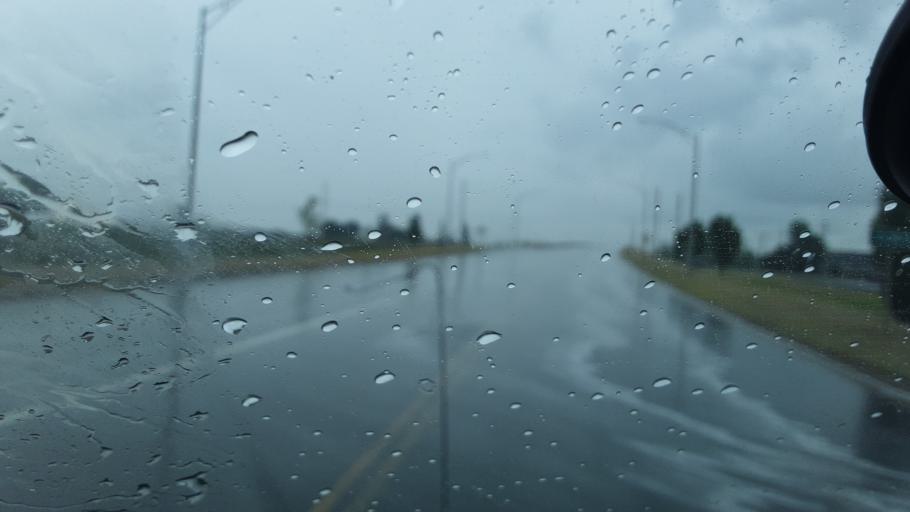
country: US
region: Ohio
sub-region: Williams County
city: Montpelier
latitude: 41.5868
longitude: -84.5855
